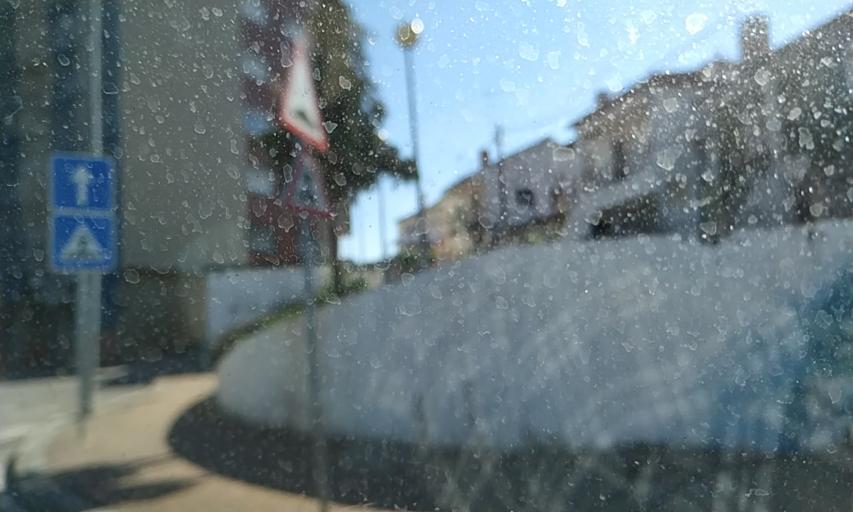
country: PT
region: Braganca
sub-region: Braganca Municipality
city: Braganca
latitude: 41.7952
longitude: -6.7706
